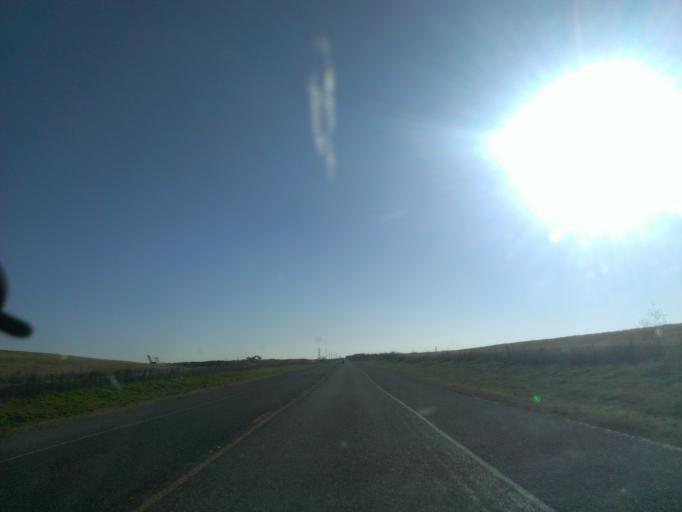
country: US
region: Texas
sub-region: Bastrop County
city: Elgin
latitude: 30.3469
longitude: -97.2767
